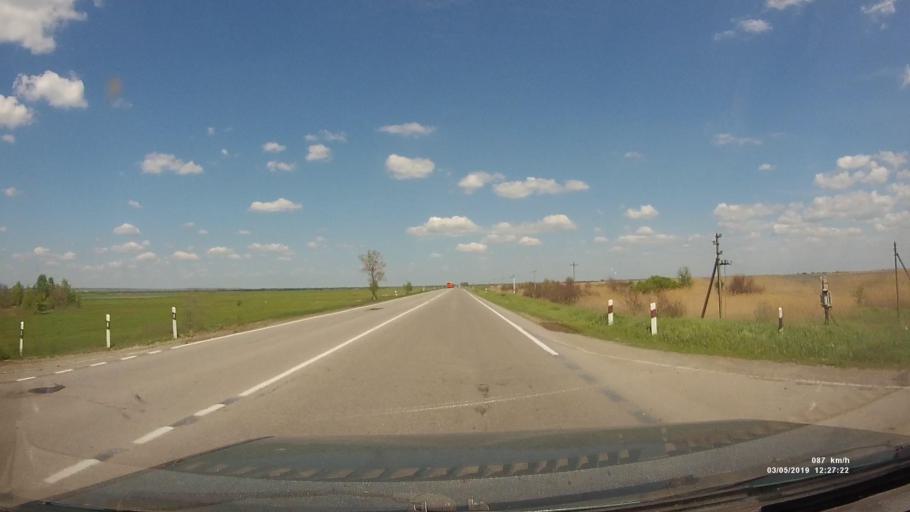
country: RU
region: Rostov
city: Semikarakorsk
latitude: 47.4585
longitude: 40.7205
